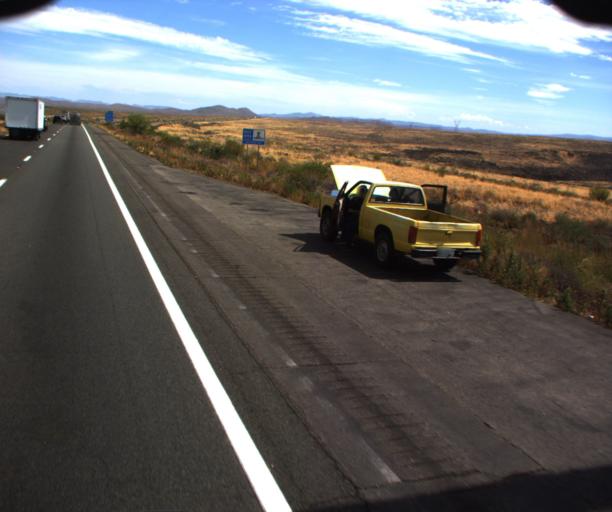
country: US
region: Arizona
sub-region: Yavapai County
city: Black Canyon City
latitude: 34.1850
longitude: -112.1333
